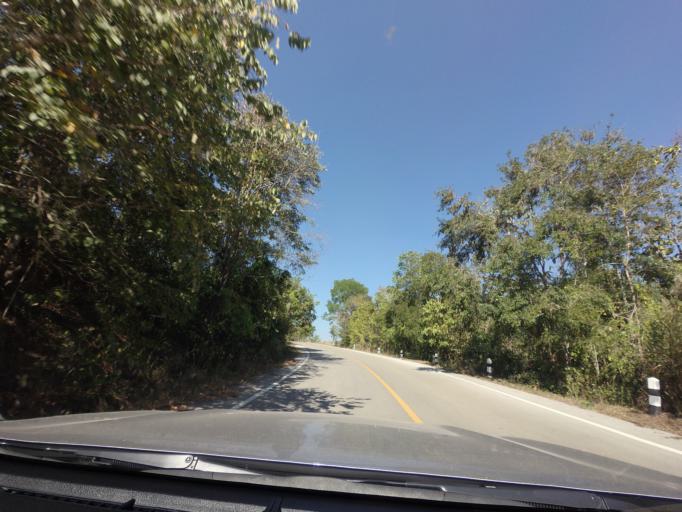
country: TH
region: Lampang
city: Chae Hom
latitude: 18.5859
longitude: 99.6263
